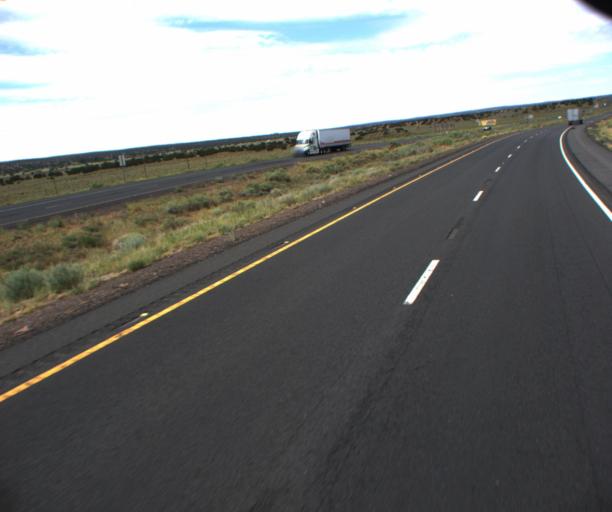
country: US
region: Arizona
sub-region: Apache County
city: Houck
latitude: 35.2802
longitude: -109.1804
